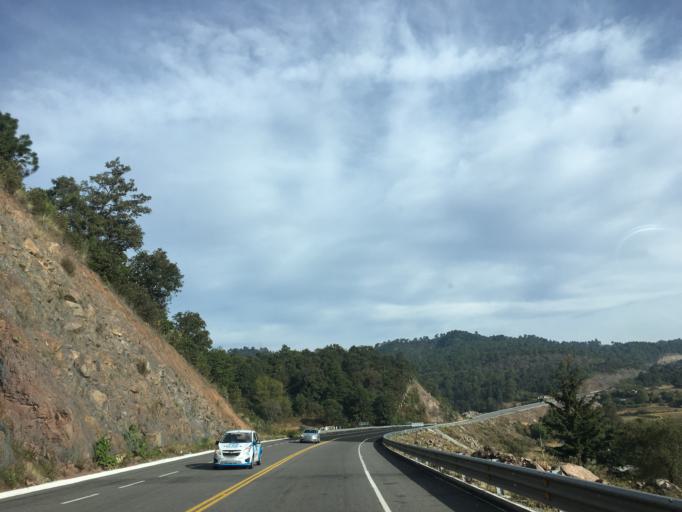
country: MX
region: Mexico
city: San Bartolo
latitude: 19.2505
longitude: -100.0675
